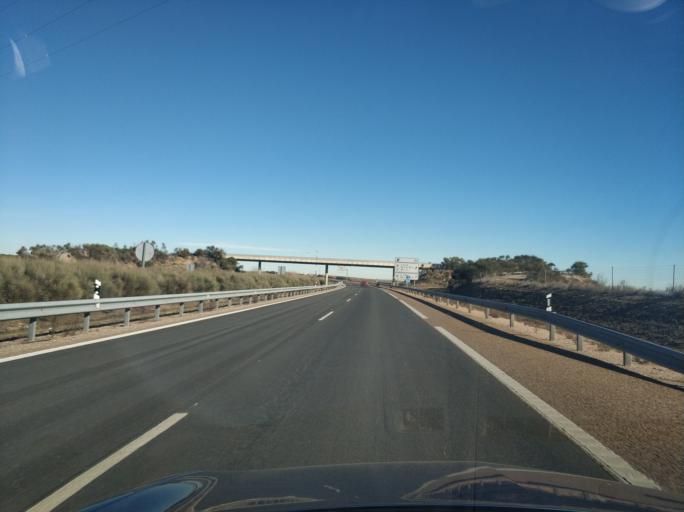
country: ES
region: Castille and Leon
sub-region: Provincia de Valladolid
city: Alaejos
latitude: 41.2956
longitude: -5.2335
